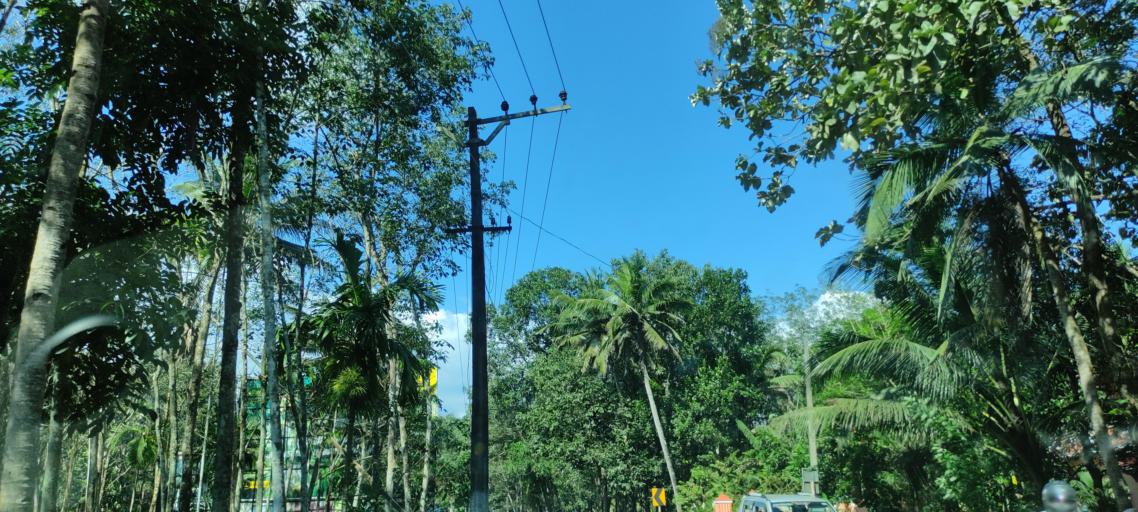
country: IN
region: Kerala
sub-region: Pattanamtitta
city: Adur
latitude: 9.1906
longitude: 76.7454
